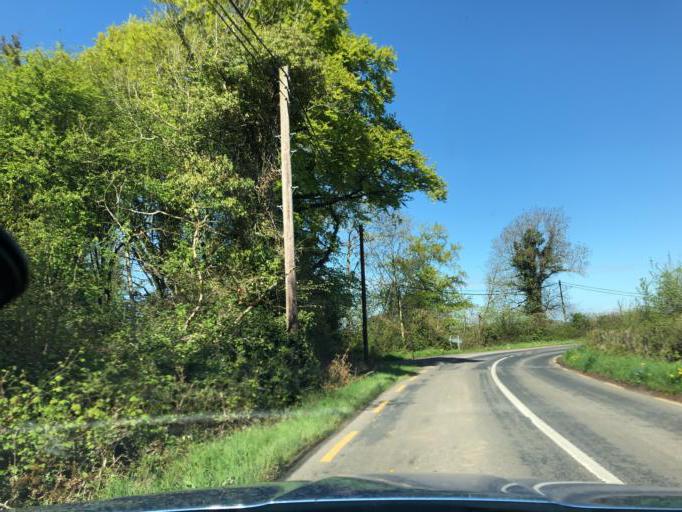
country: IE
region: Connaught
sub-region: County Galway
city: Portumna
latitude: 53.1277
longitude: -8.3501
